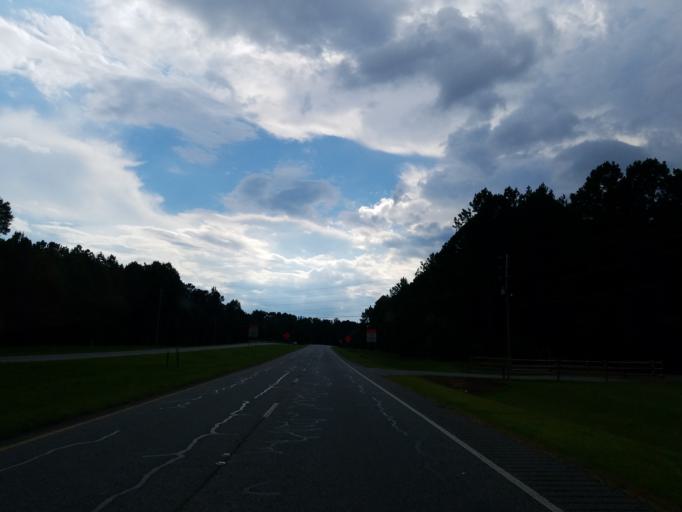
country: US
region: Georgia
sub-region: Chattooga County
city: Summerville
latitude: 34.4117
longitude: -85.2232
